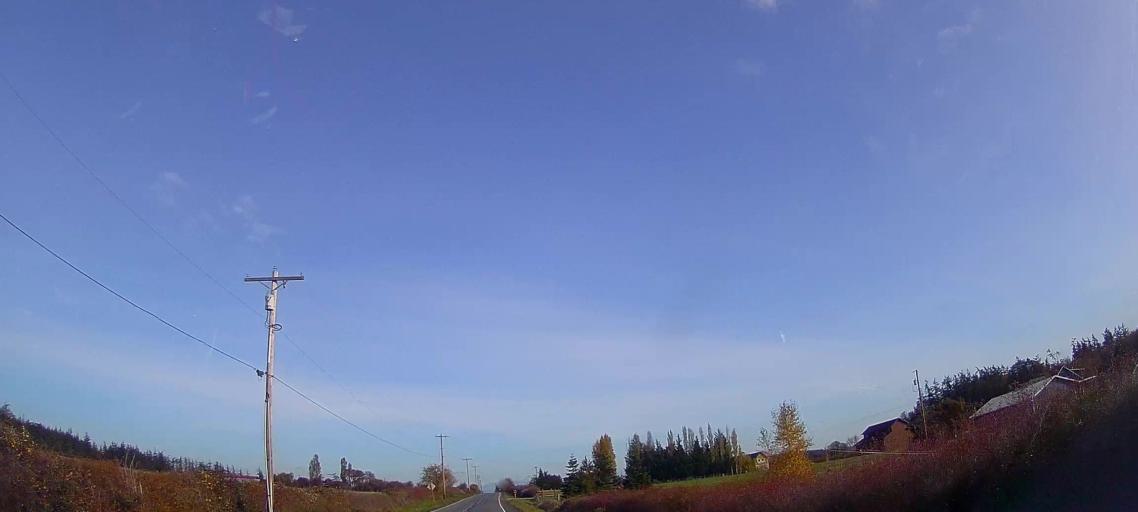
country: US
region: Washington
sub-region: Snohomish County
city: Stanwood
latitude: 48.2545
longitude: -122.4487
